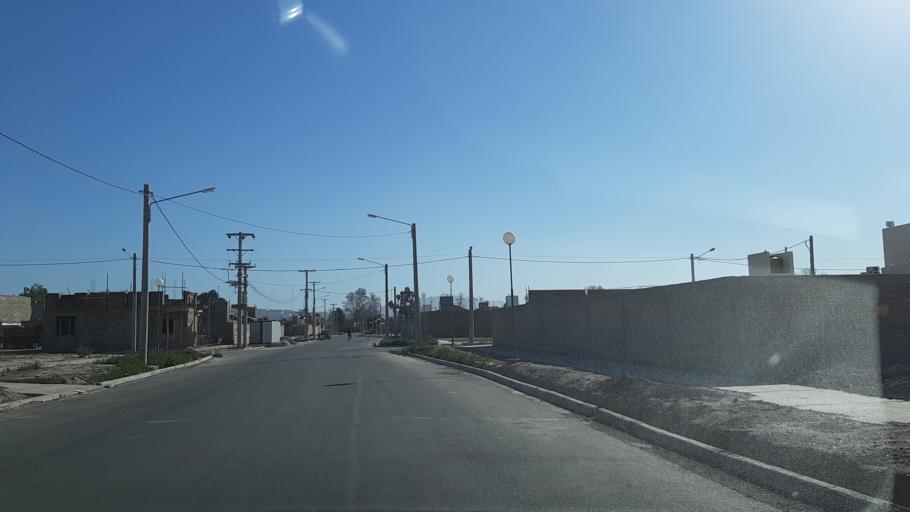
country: AR
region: San Juan
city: San Juan
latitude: -31.5192
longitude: -68.5911
